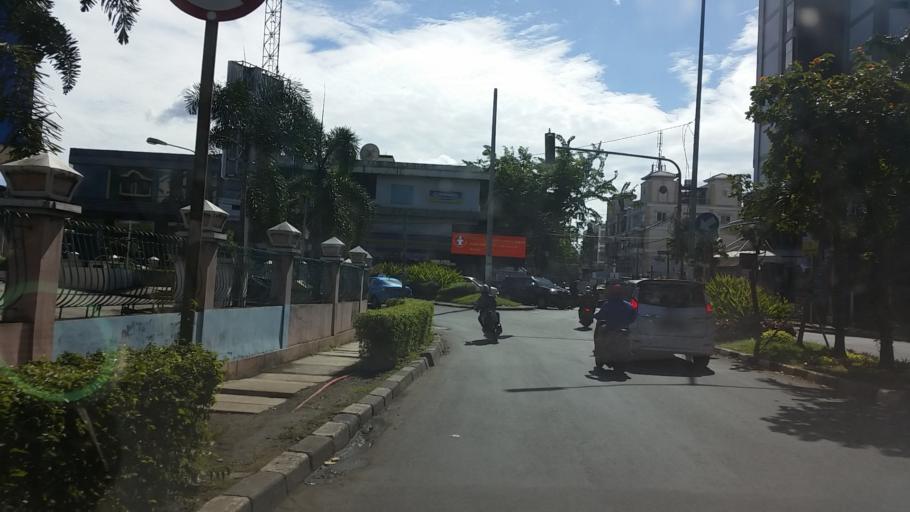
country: ID
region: Banten
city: South Tangerang
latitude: -6.2634
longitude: 106.7878
